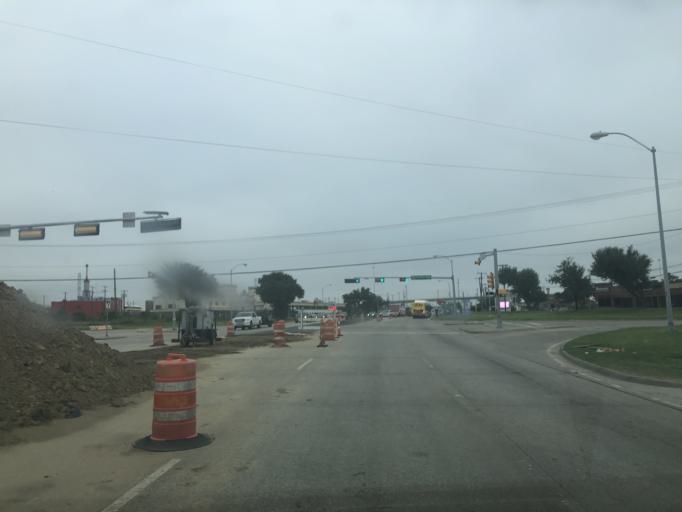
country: US
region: Texas
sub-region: Dallas County
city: Farmers Branch
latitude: 32.8620
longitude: -96.8809
